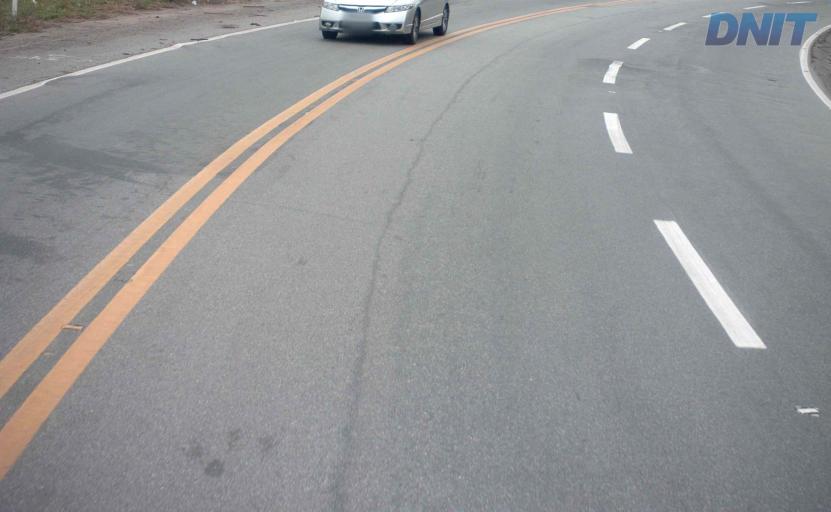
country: BR
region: Minas Gerais
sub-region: Timoteo
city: Timoteo
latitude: -19.6371
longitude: -42.8074
